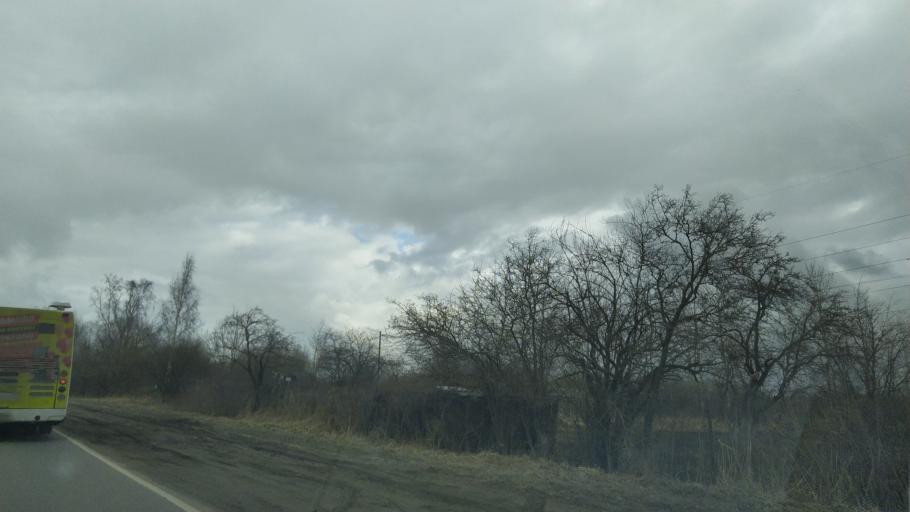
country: RU
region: St.-Petersburg
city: Tyarlevo
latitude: 59.7151
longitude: 30.4363
